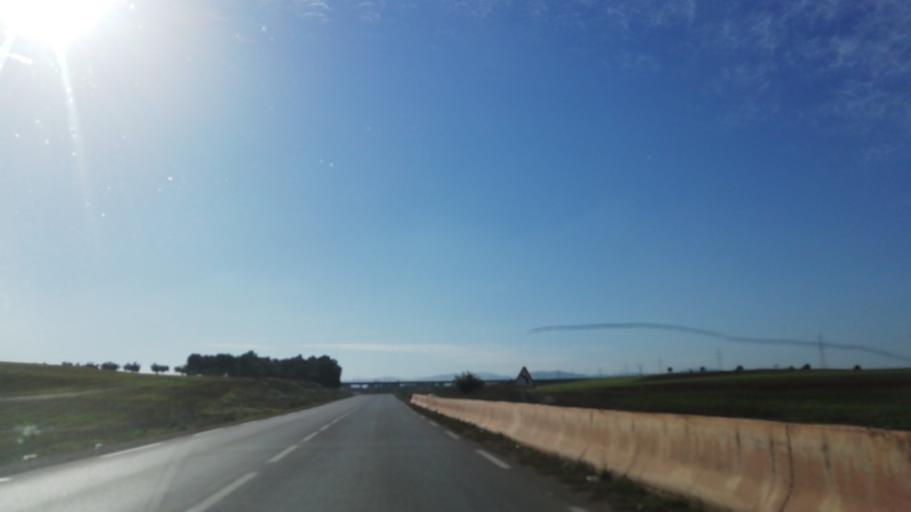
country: DZ
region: Tlemcen
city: Ouled Mimoun
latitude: 35.0147
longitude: -0.9052
